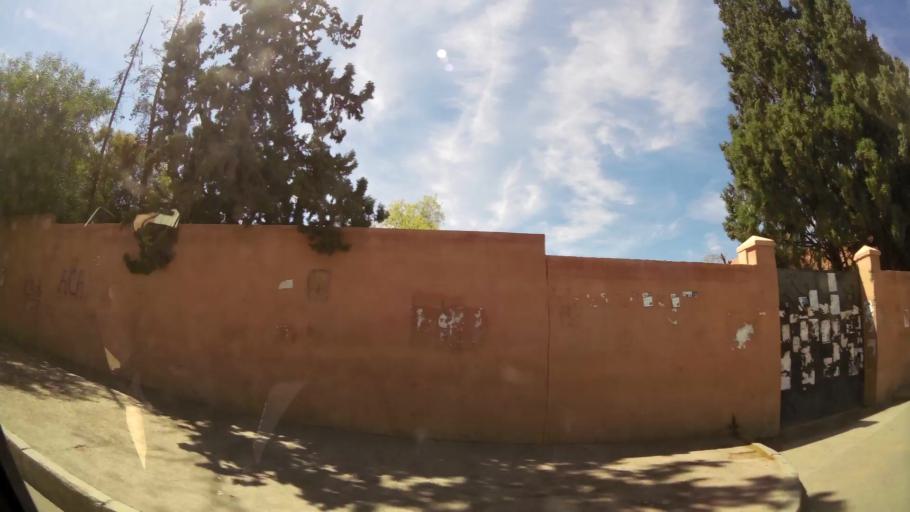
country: MA
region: Marrakech-Tensift-Al Haouz
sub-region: Marrakech
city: Marrakesh
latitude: 31.6636
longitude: -7.9986
